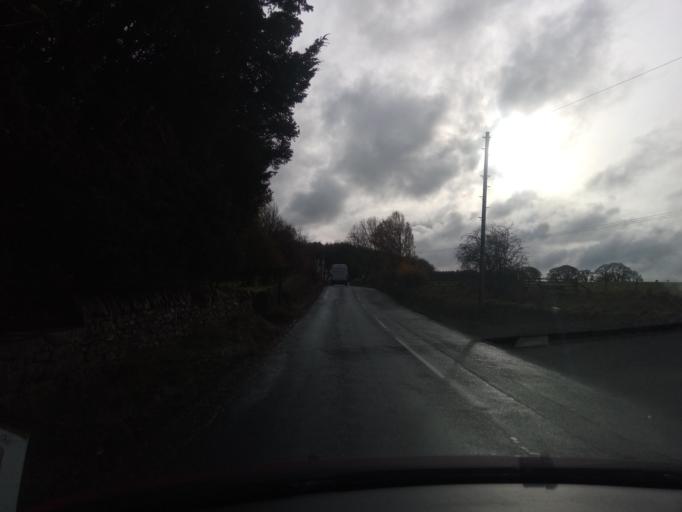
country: GB
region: England
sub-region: Northumberland
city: Birtley
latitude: 55.0598
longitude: -2.1925
